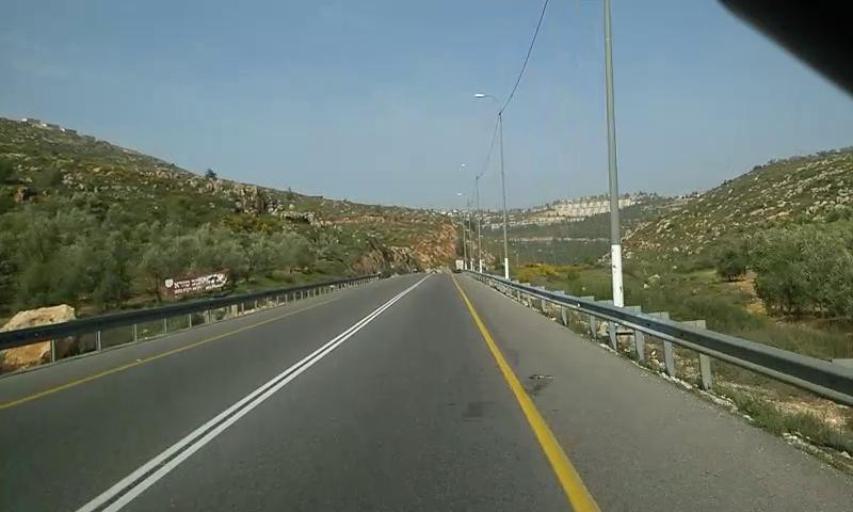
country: PS
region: West Bank
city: Qaryut
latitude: 32.0638
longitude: 35.2760
